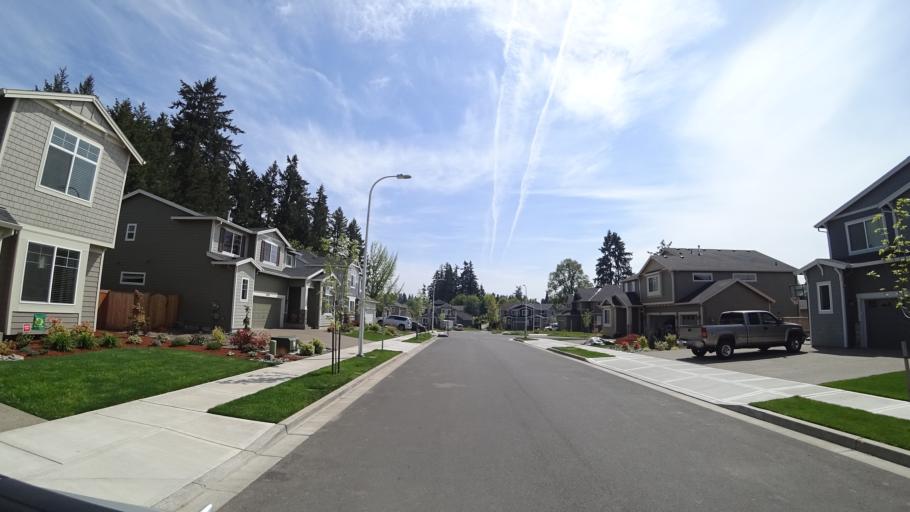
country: US
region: Oregon
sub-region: Washington County
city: Hillsboro
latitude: 45.5126
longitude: -122.9348
